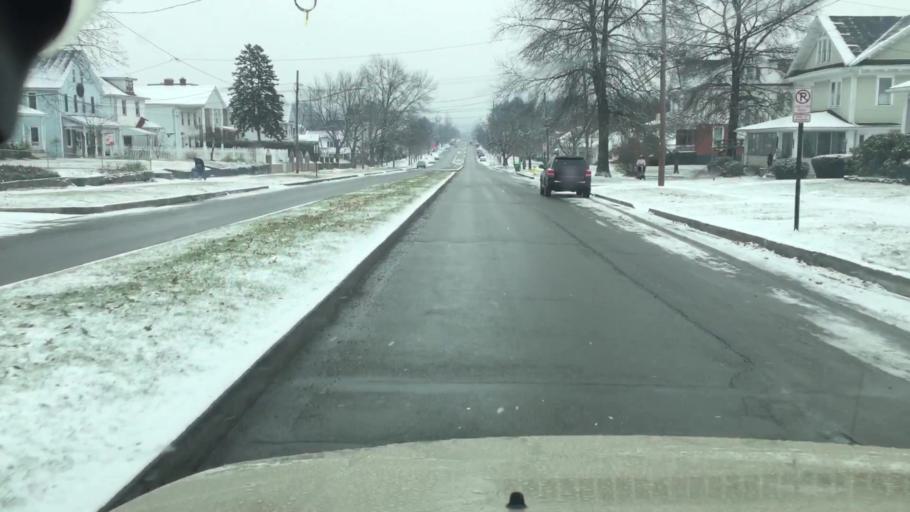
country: US
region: Pennsylvania
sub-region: Columbia County
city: Berwick
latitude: 41.0630
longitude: -76.2407
